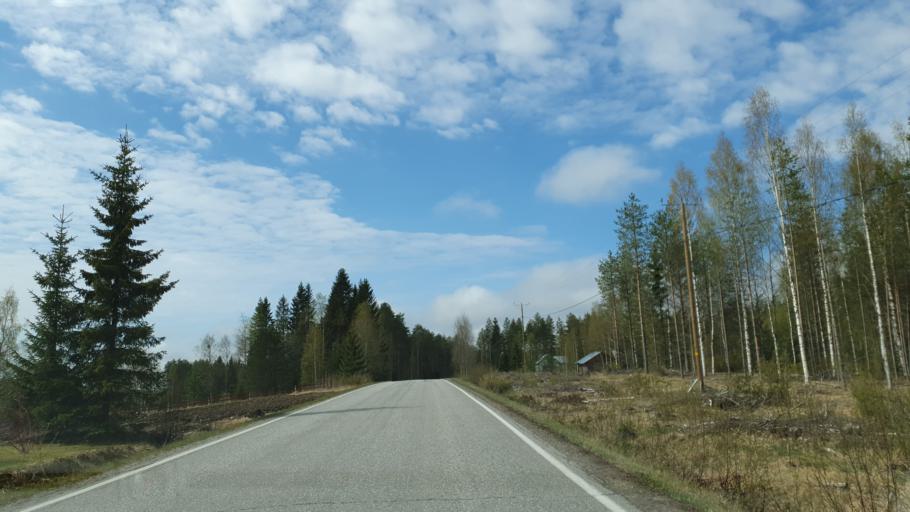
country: FI
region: Kainuu
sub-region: Kehys-Kainuu
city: Kuhmo
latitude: 64.1226
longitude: 29.6603
